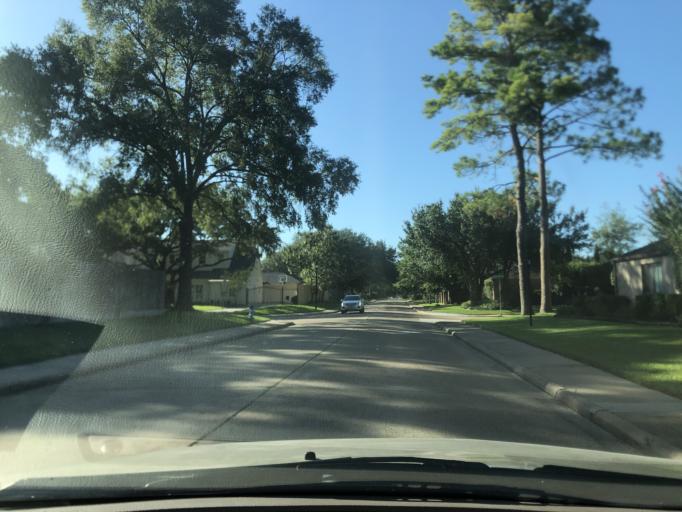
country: US
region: Texas
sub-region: Harris County
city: Bunker Hill Village
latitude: 29.7469
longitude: -95.5534
